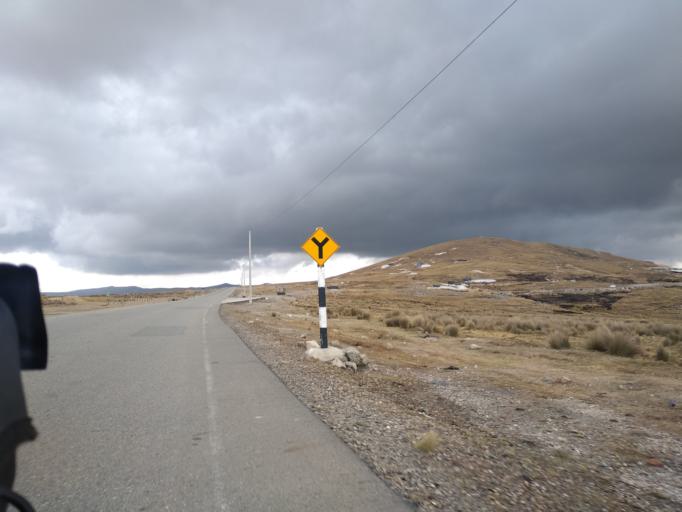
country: PE
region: La Libertad
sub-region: Provincia de Santiago de Chuco
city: Quiruvilca
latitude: -7.9925
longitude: -78.2927
